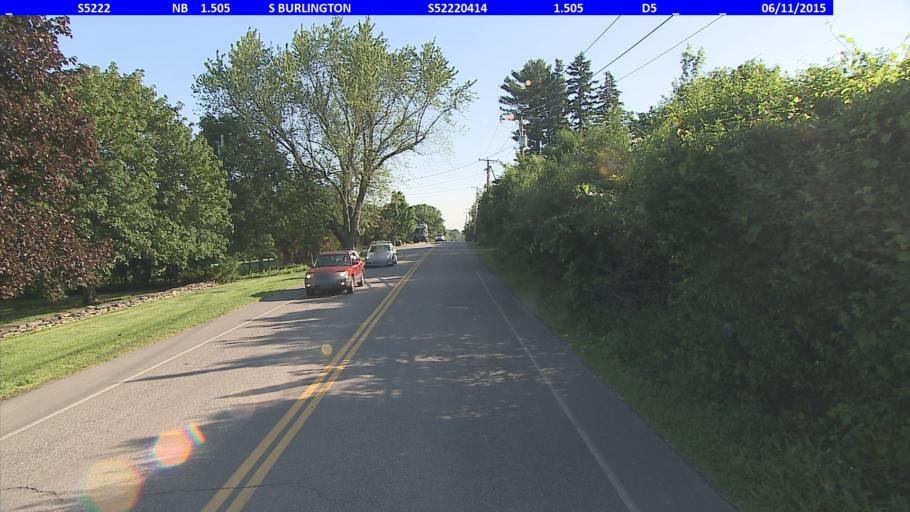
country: US
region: Vermont
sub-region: Chittenden County
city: South Burlington
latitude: 44.4383
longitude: -73.1907
